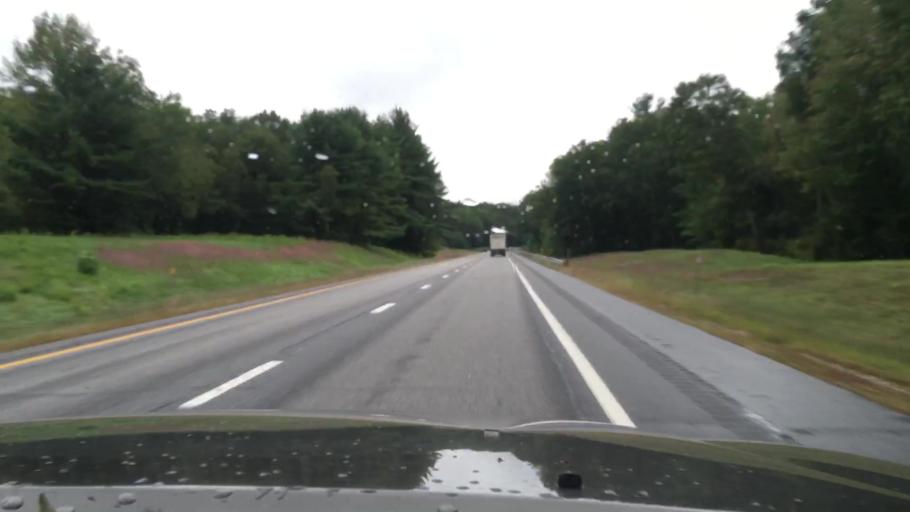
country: US
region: New Hampshire
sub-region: Merrimack County
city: East Concord
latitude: 43.2675
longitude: -71.5570
